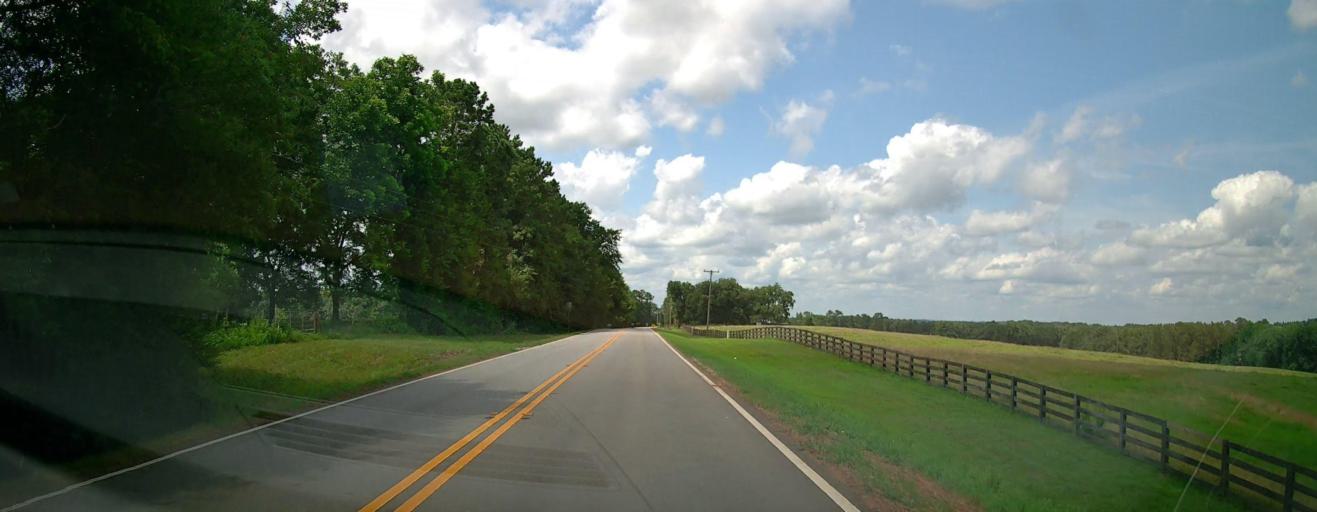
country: US
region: Georgia
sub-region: Carroll County
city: Bowdon
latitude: 33.4654
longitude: -85.2952
